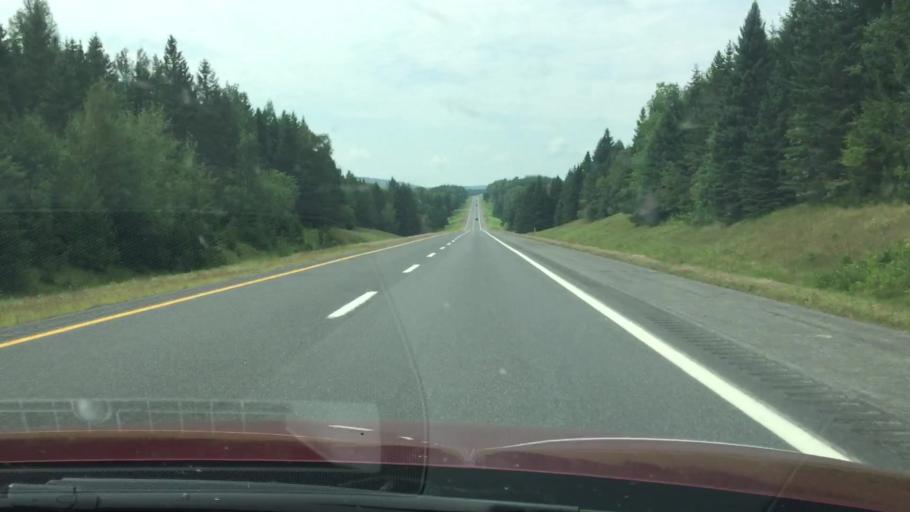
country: US
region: Maine
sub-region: Aroostook County
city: Houlton
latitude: 46.1412
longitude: -67.9782
